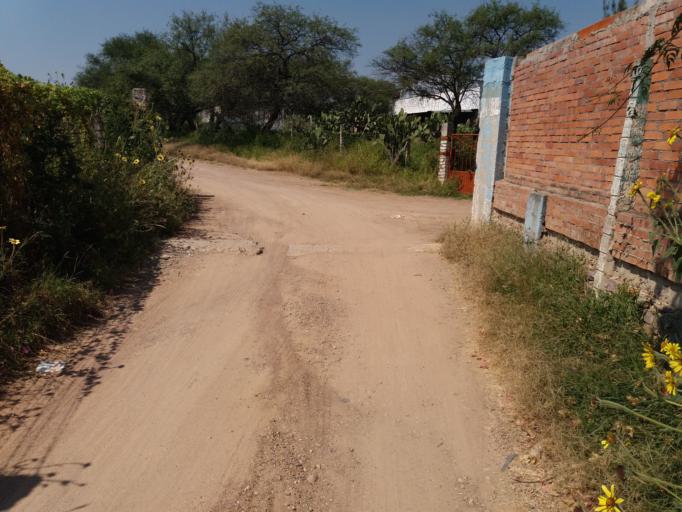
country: MX
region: Aguascalientes
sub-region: Aguascalientes
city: Penuelas (El Cienegal)
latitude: 21.7603
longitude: -102.2688
